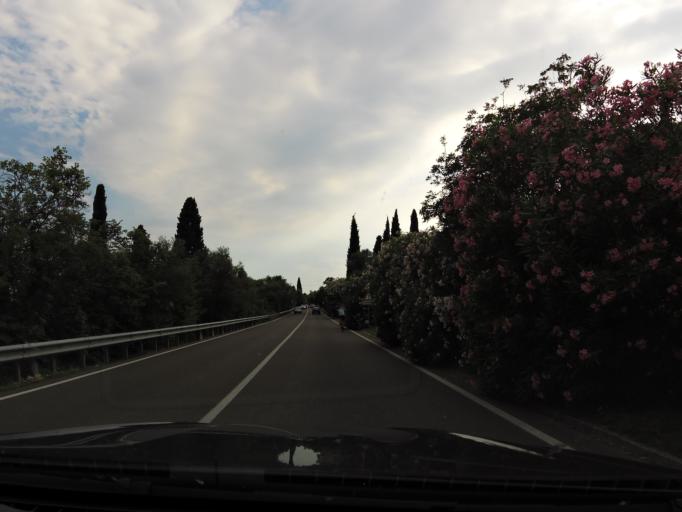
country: IT
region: Veneto
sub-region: Provincia di Verona
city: Torri del Benaco
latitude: 45.5757
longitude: 10.6793
